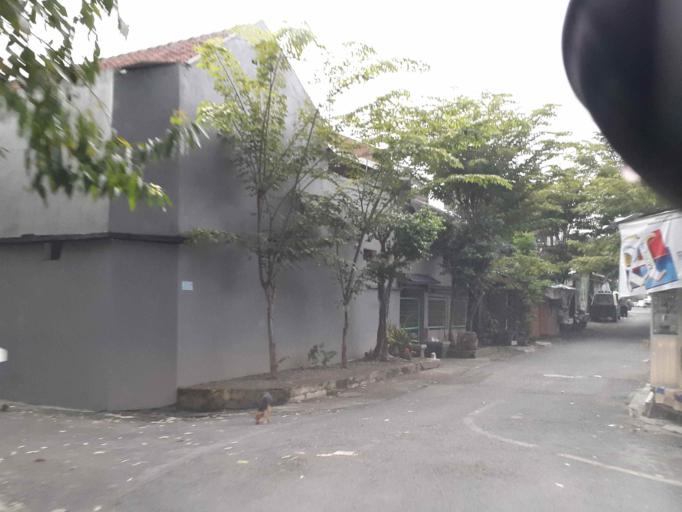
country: ID
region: Central Java
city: Surakarta
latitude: -7.5546
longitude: 110.8148
